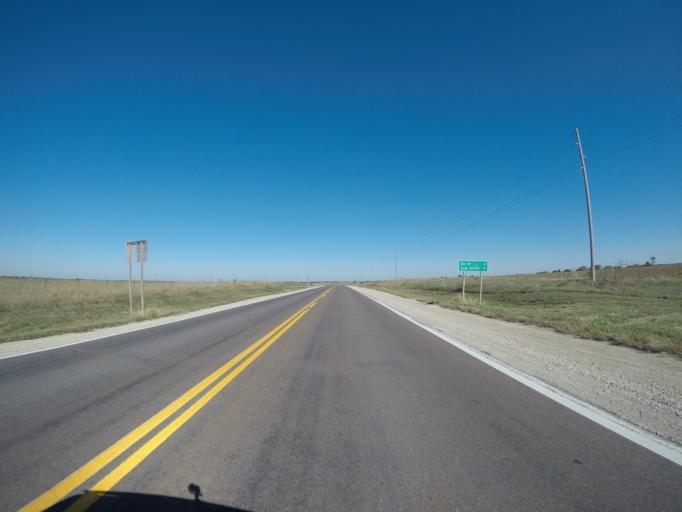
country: US
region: Kansas
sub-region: Clay County
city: Clay Center
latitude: 39.3091
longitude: -96.9236
